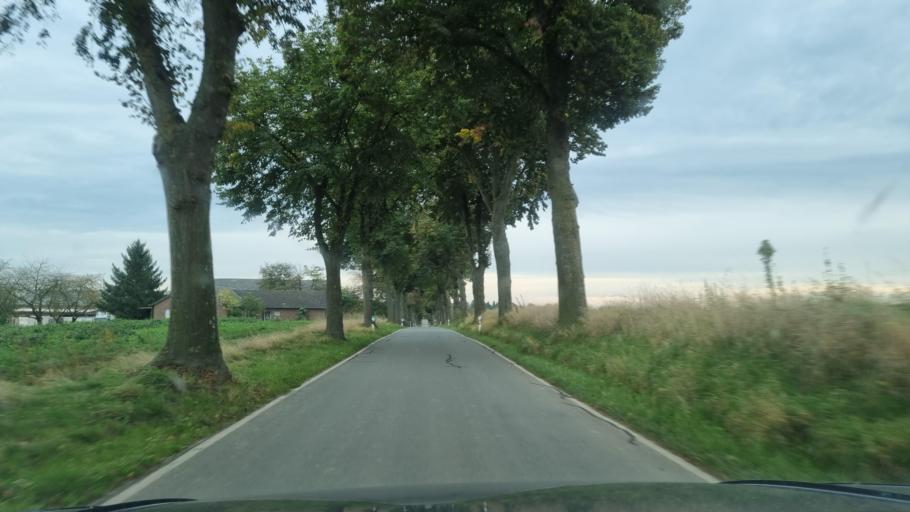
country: DE
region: North Rhine-Westphalia
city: Kalkar
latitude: 51.7351
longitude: 6.2205
